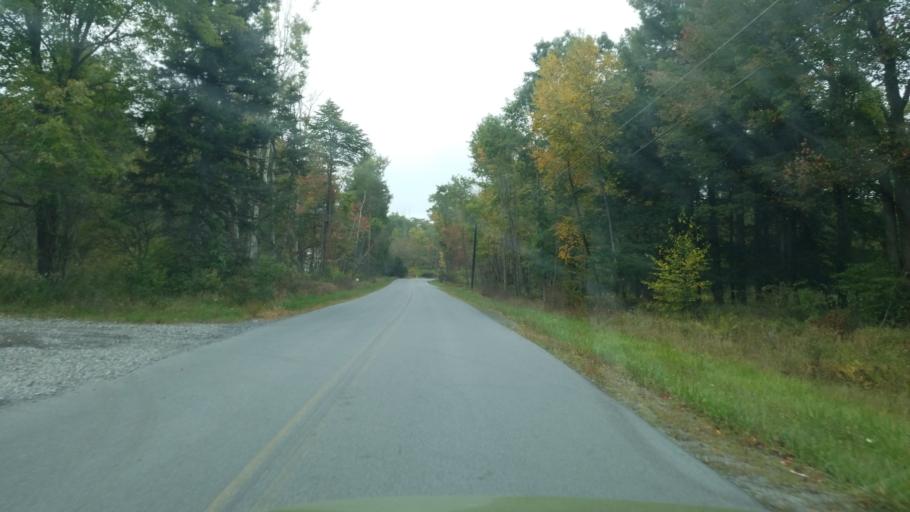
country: US
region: Pennsylvania
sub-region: Clearfield County
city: Curwensville
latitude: 41.0227
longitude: -78.5546
